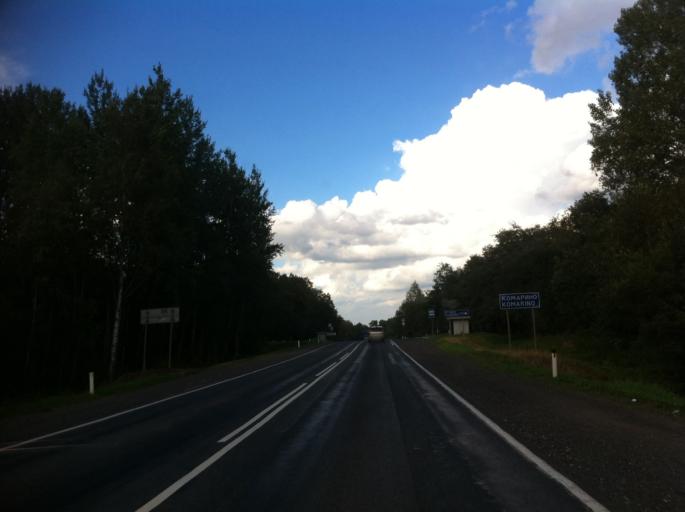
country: RU
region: Pskov
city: Strugi-Krasnyye
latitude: 58.1912
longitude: 29.2778
